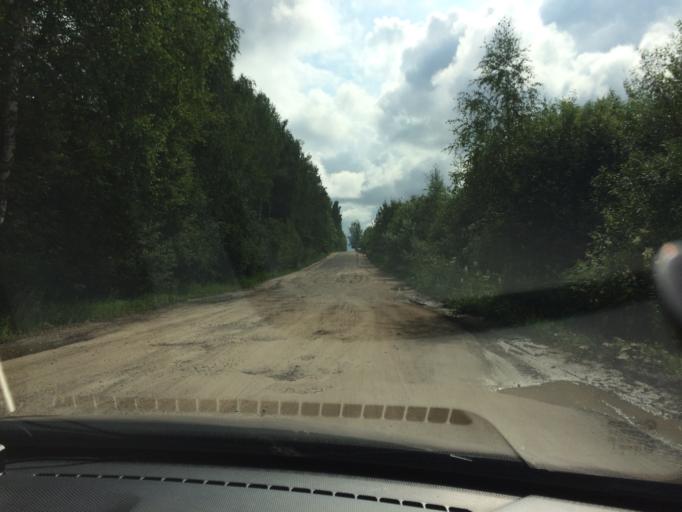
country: RU
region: Mariy-El
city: Mochalishche
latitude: 56.5461
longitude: 48.3770
